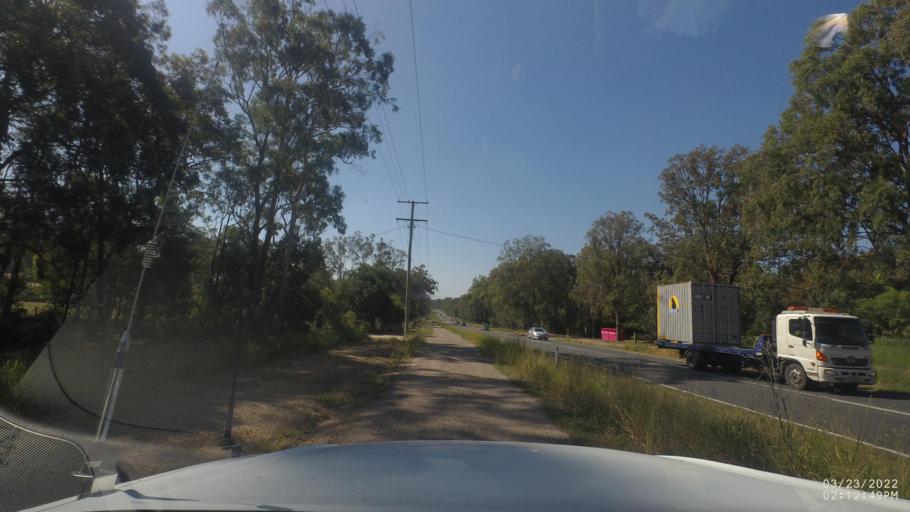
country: AU
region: Queensland
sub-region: Logan
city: Logan Reserve
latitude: -27.7405
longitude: 153.1258
